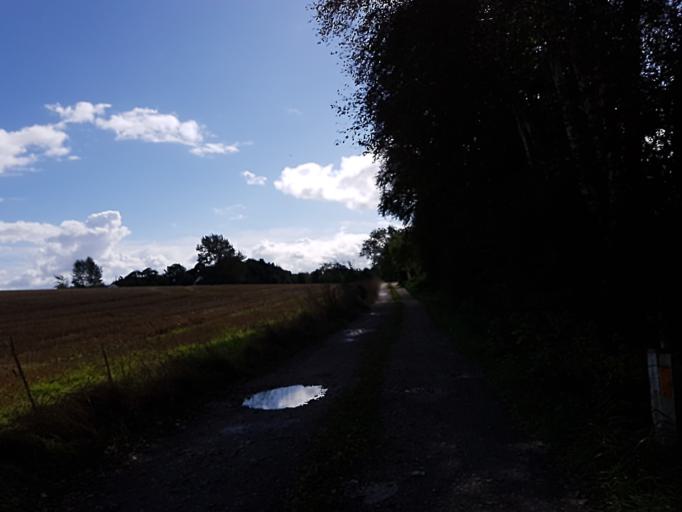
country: DK
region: Capital Region
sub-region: Egedal Kommune
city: Olstykke
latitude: 55.7884
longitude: 12.1263
